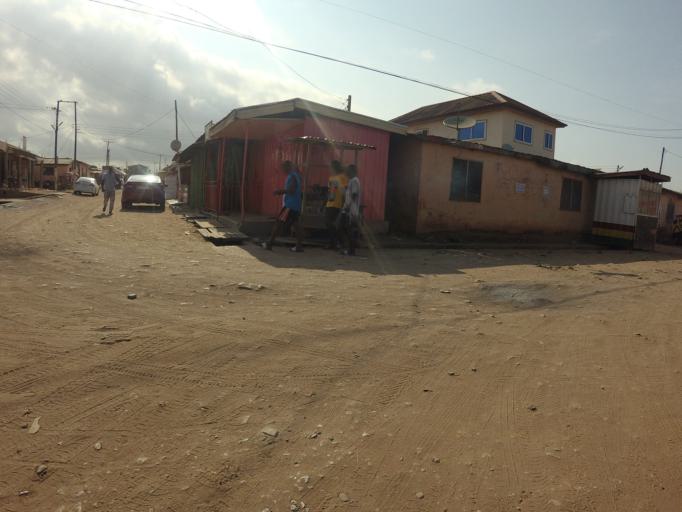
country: GH
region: Greater Accra
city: Dome
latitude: 5.6566
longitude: -0.2680
